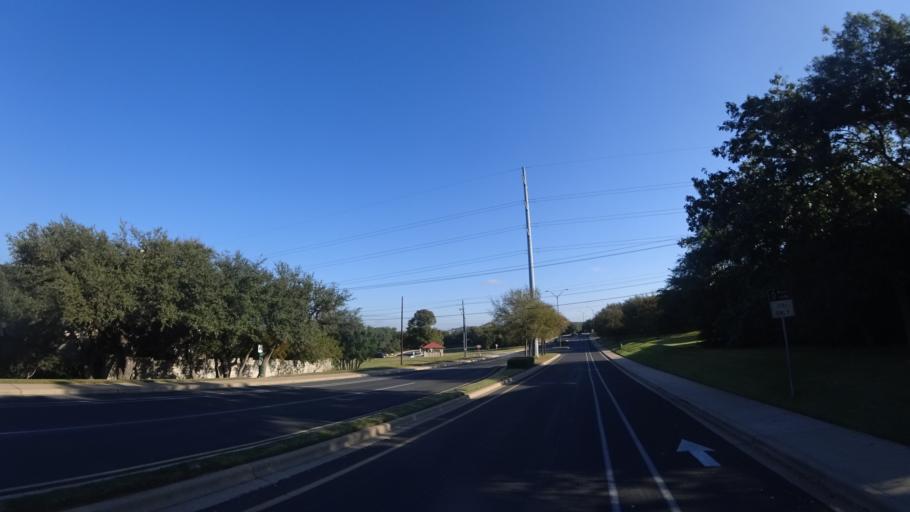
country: US
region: Texas
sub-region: Travis County
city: Hudson Bend
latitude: 30.3754
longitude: -97.8936
